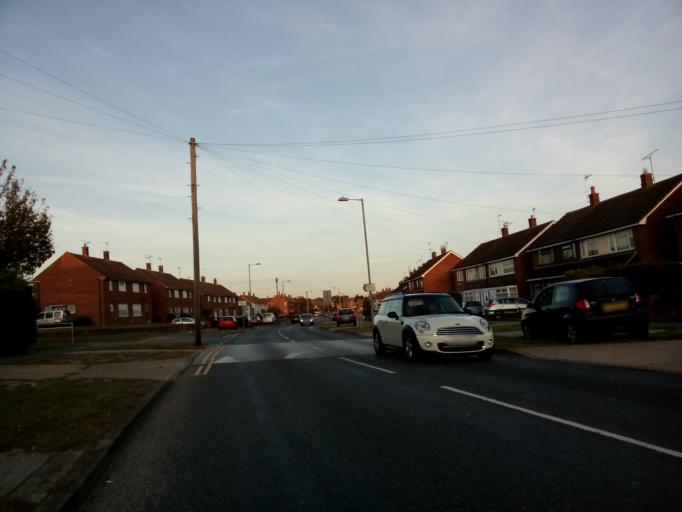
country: GB
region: England
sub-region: Suffolk
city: Bramford
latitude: 52.0438
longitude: 1.1136
